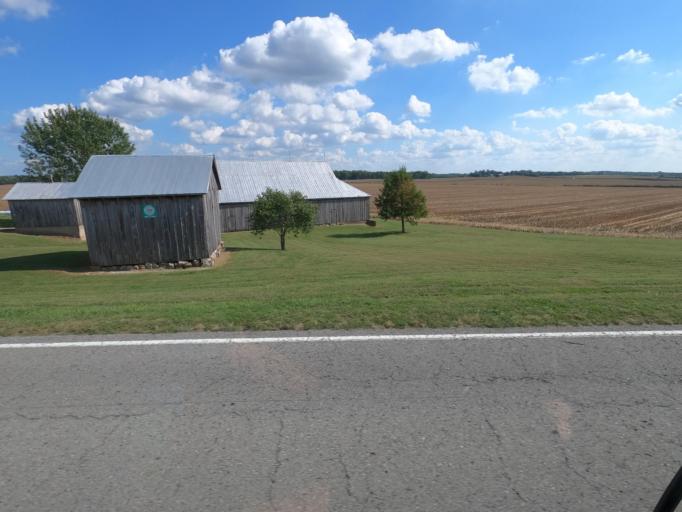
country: US
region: Illinois
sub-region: Massac County
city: Metropolis
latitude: 37.2691
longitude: -88.7596
